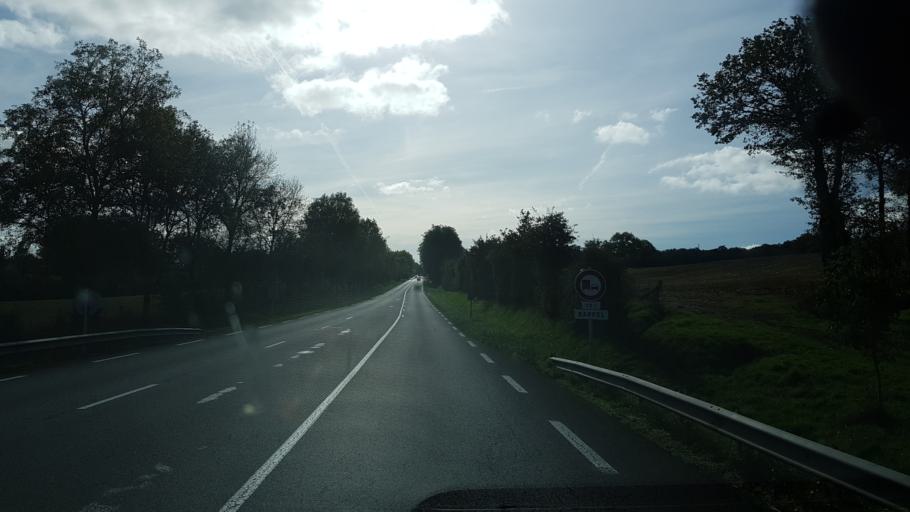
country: FR
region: Poitou-Charentes
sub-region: Departement de la Charente
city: Confolens
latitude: 46.0022
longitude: 0.6353
